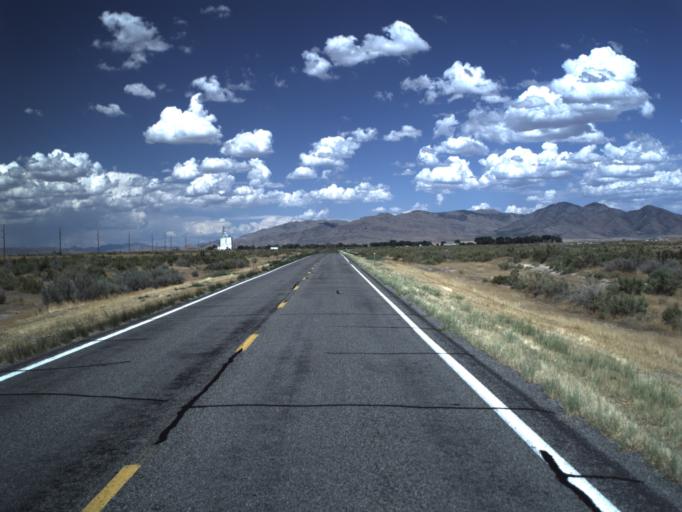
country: US
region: Utah
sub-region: Millard County
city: Delta
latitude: 39.4997
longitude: -112.3928
